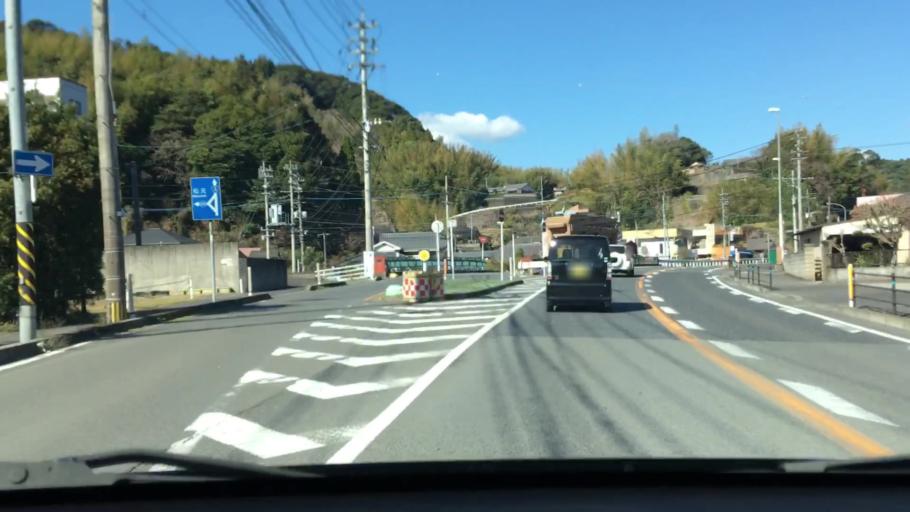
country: JP
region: Kagoshima
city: Ijuin
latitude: 31.6558
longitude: 130.4963
